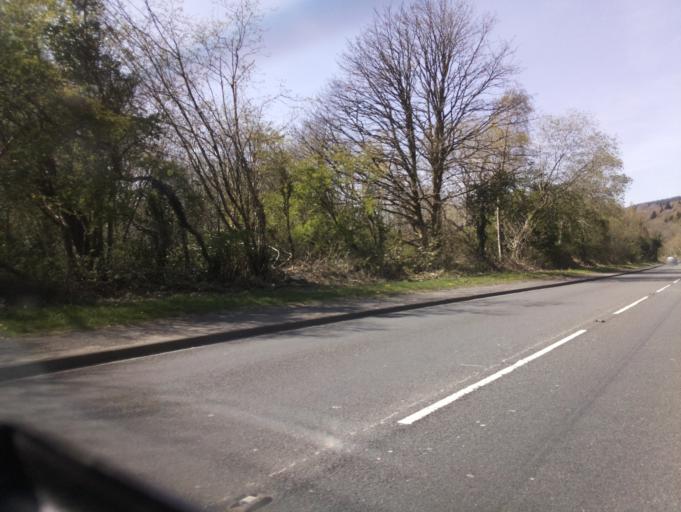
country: GB
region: Wales
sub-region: Merthyr Tydfil County Borough
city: Treharris
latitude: 51.6600
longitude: -3.3389
